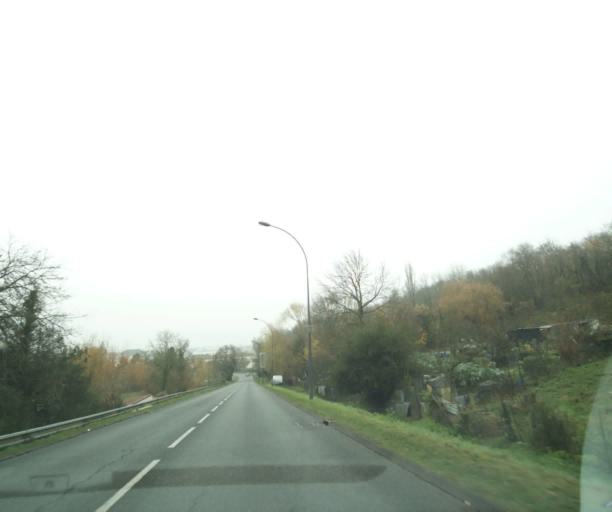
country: FR
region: Ile-de-France
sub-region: Departement de Seine-Saint-Denis
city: Vaujours
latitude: 48.9274
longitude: 2.5697
